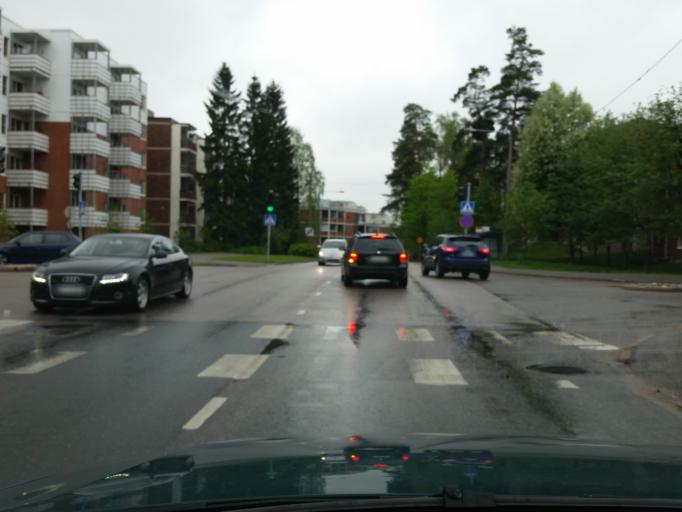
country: FI
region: Uusimaa
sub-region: Helsinki
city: Kilo
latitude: 60.2289
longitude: 24.8137
